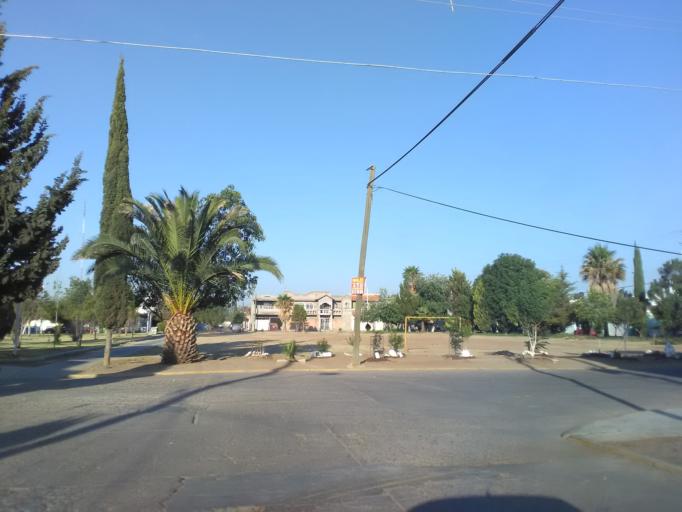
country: MX
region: Durango
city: Victoria de Durango
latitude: 24.0551
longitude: -104.6248
